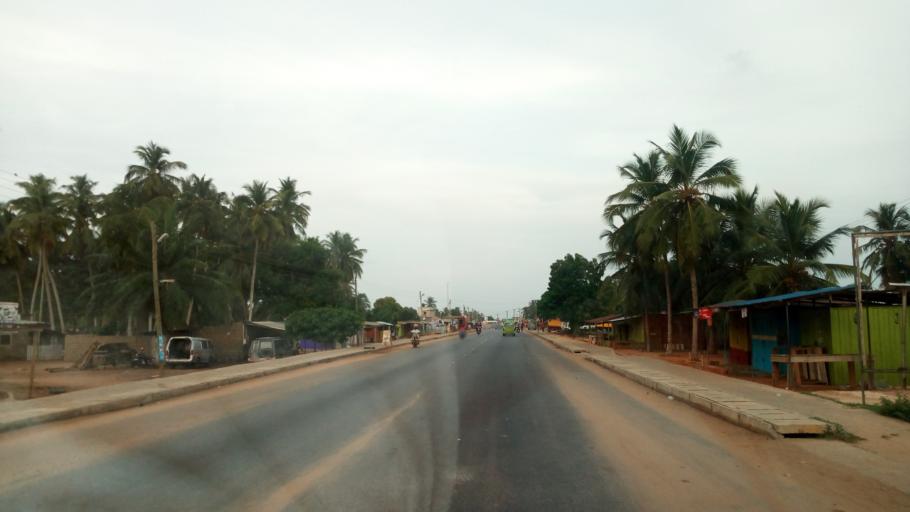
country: TG
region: Maritime
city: Lome
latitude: 6.1139
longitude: 1.1669
